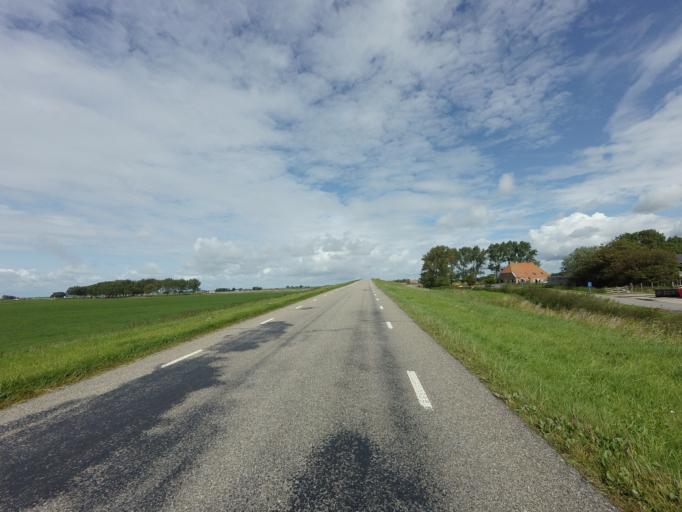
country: NL
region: Friesland
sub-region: Sudwest Fryslan
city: Makkum
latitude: 53.0913
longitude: 5.4205
